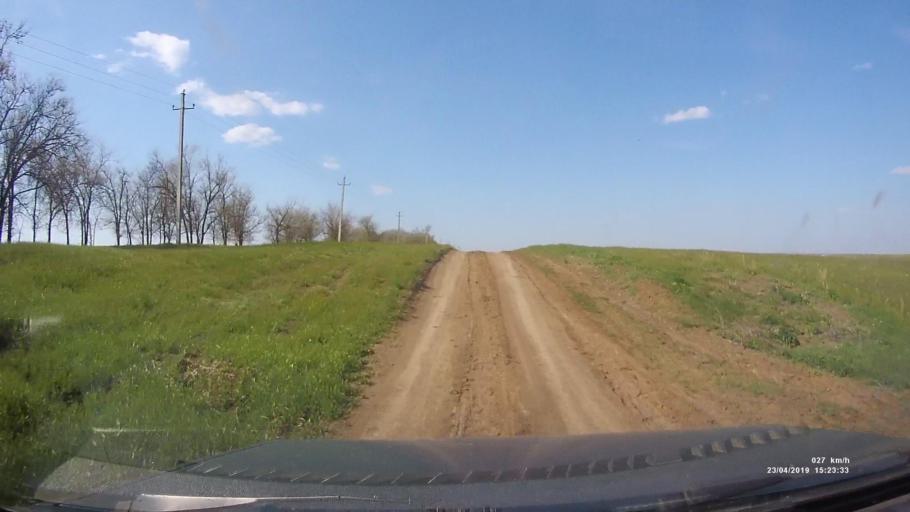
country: RU
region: Rostov
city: Remontnoye
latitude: 46.5363
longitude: 42.9697
